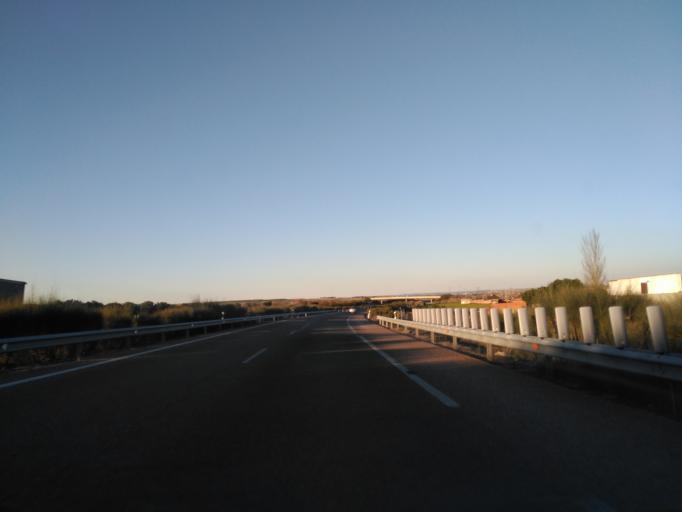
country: ES
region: Castille and Leon
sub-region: Provincia de Valladolid
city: Alaejos
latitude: 41.3065
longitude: -5.2281
